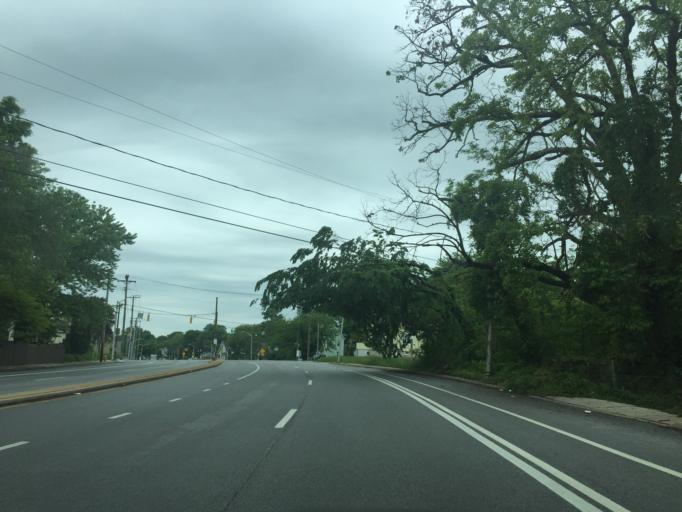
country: US
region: Maryland
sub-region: Baltimore County
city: Parkville
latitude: 39.3472
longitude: -76.5535
